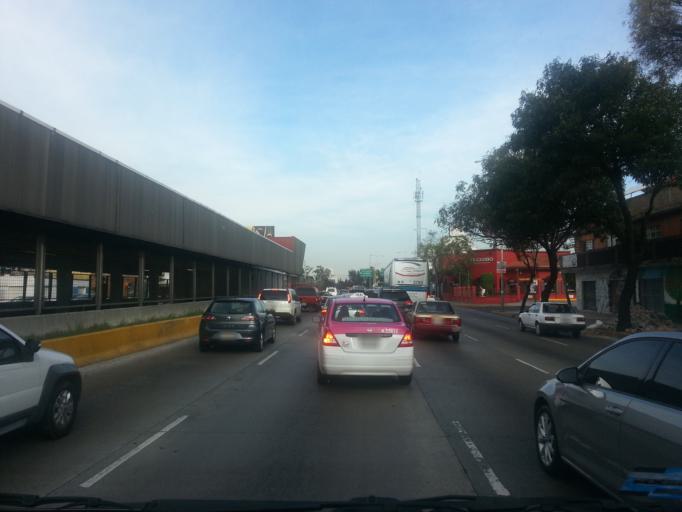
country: MX
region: Mexico City
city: Venustiano Carranza
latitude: 19.4516
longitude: -99.1054
